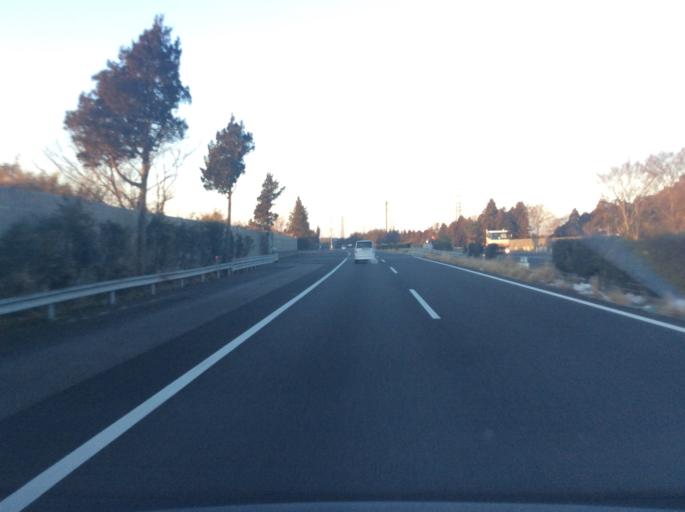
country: JP
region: Ibaraki
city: Hitachi-Naka
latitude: 36.4453
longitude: 140.4603
